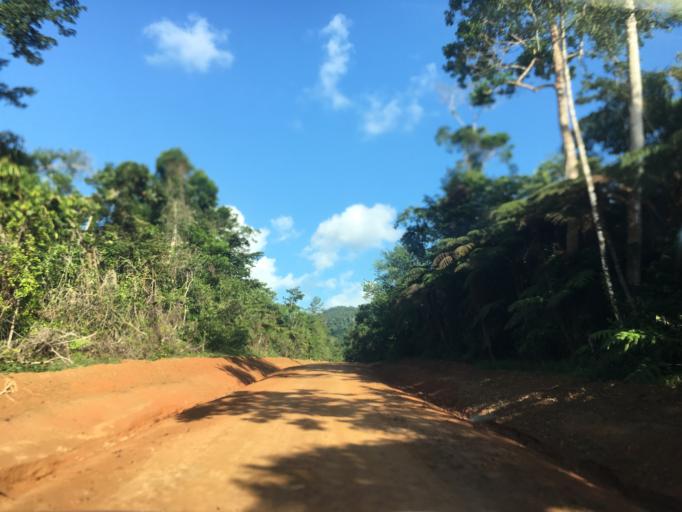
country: BZ
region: Stann Creek
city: Placencia
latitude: 16.7839
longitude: -88.4562
